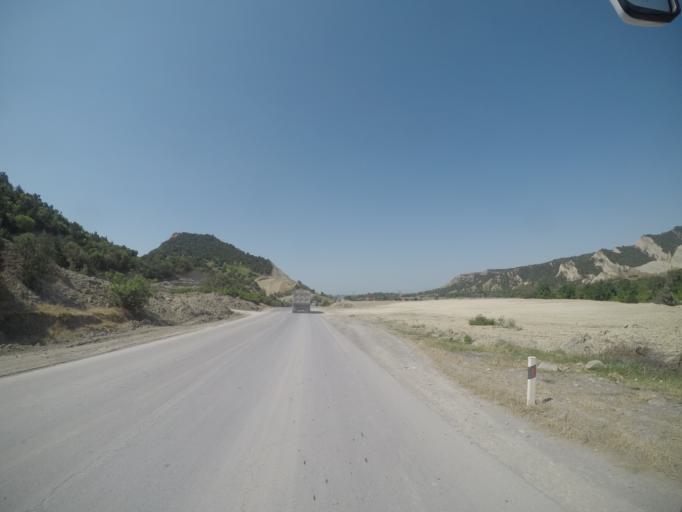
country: AZ
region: Agdas
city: Agdas
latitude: 40.7203
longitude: 47.5615
